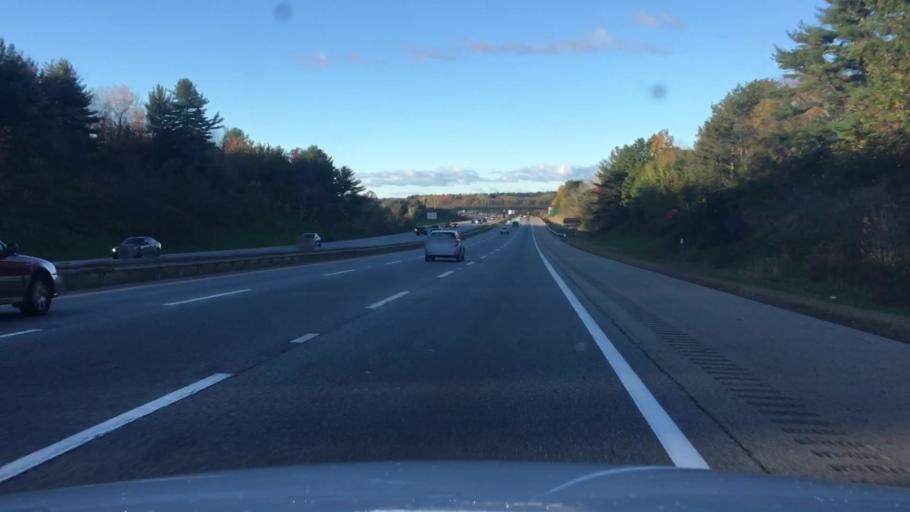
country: US
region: Maine
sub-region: York County
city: Biddeford
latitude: 43.5073
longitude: -70.4797
